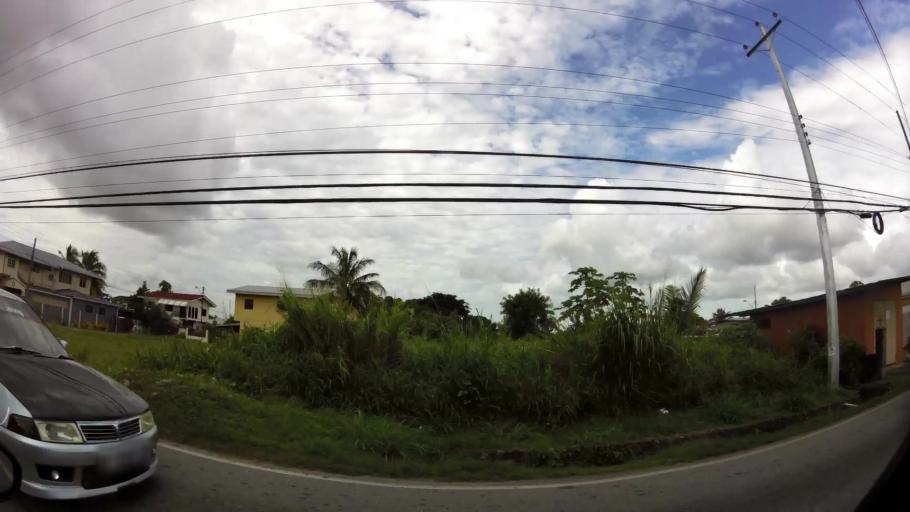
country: TT
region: Chaguanas
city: Chaguanas
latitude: 10.4838
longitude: -61.4080
